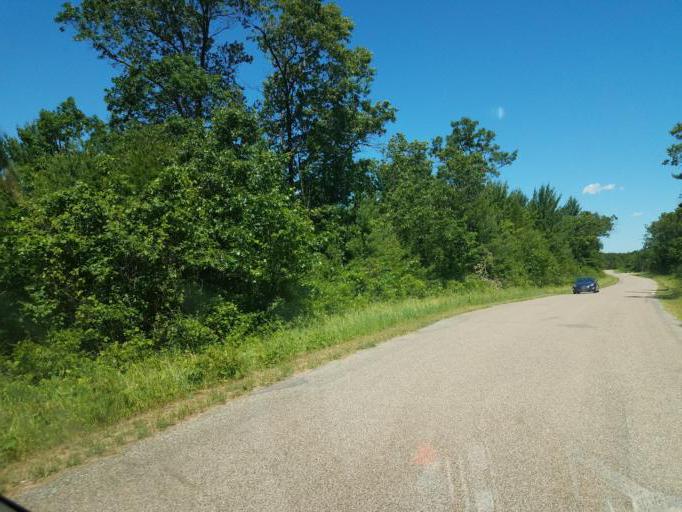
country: US
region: Wisconsin
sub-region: Adams County
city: Friendship
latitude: 44.0229
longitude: -89.9566
